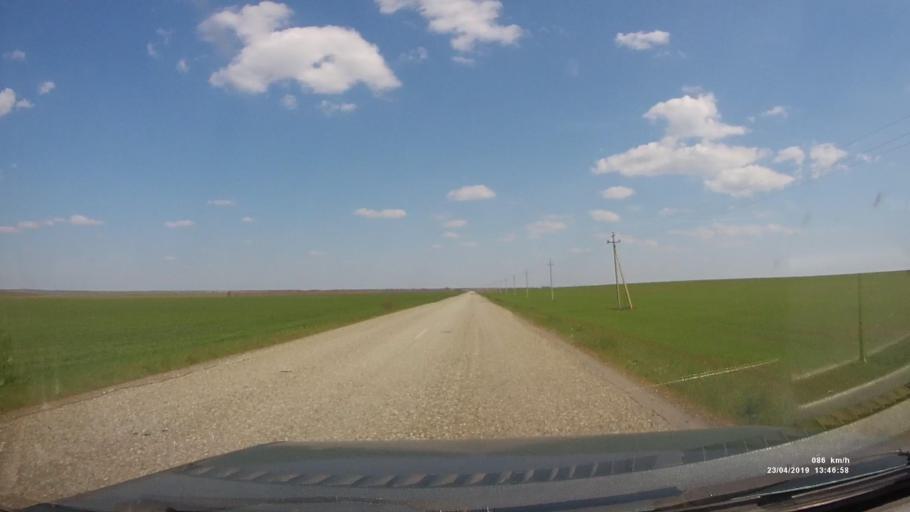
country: RU
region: Kalmykiya
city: Yashalta
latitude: 46.5999
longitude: 42.8447
